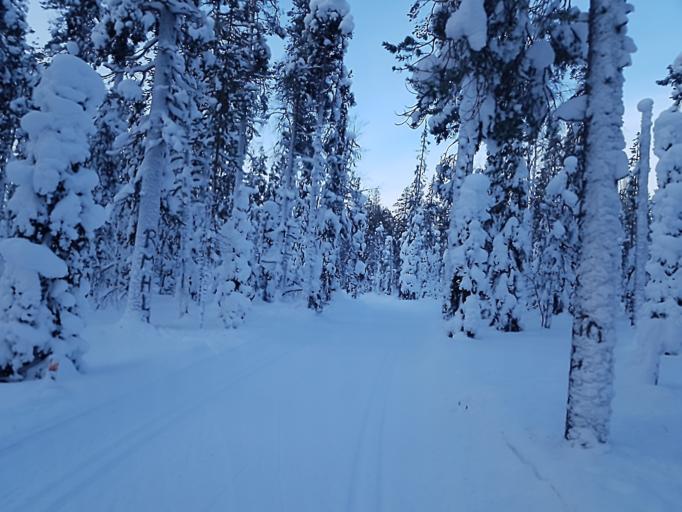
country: FI
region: Lapland
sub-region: Tunturi-Lappi
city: Kolari
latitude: 67.6385
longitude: 24.2307
